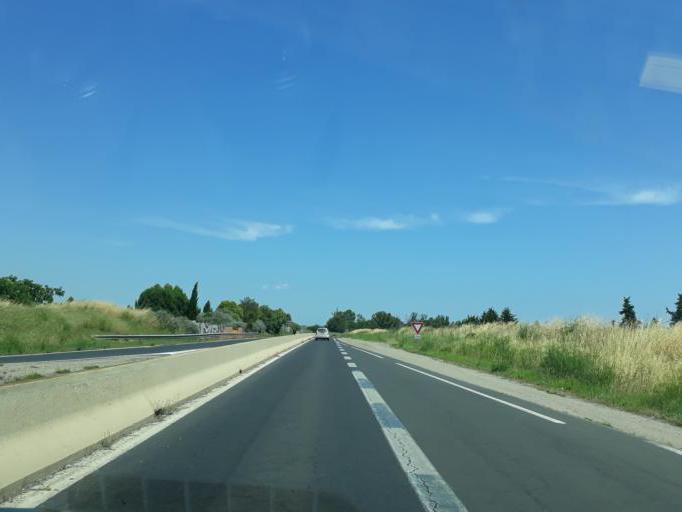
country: FR
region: Languedoc-Roussillon
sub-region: Departement de l'Herault
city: Vias
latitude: 43.3063
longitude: 3.4203
